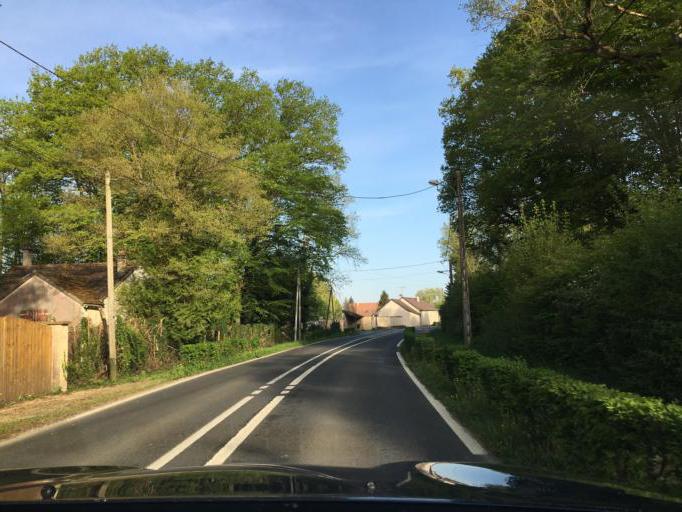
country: FR
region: Centre
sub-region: Departement d'Eure-et-Loir
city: Epernon
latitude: 48.6544
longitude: 1.6789
